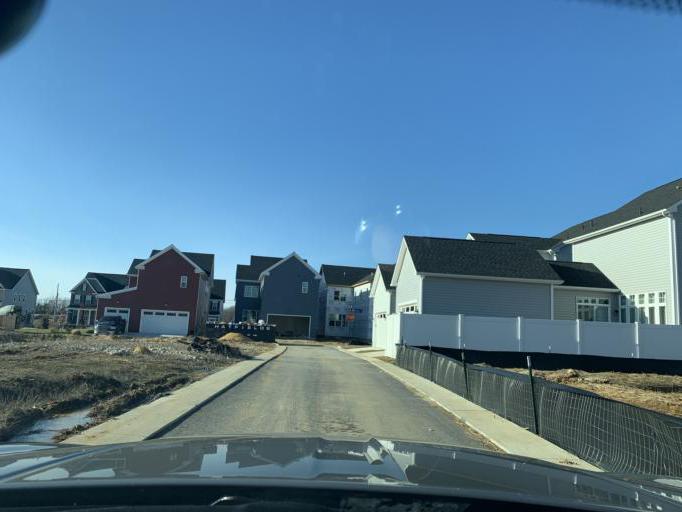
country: US
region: Maryland
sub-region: Anne Arundel County
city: Crofton
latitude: 39.0224
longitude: -76.7267
